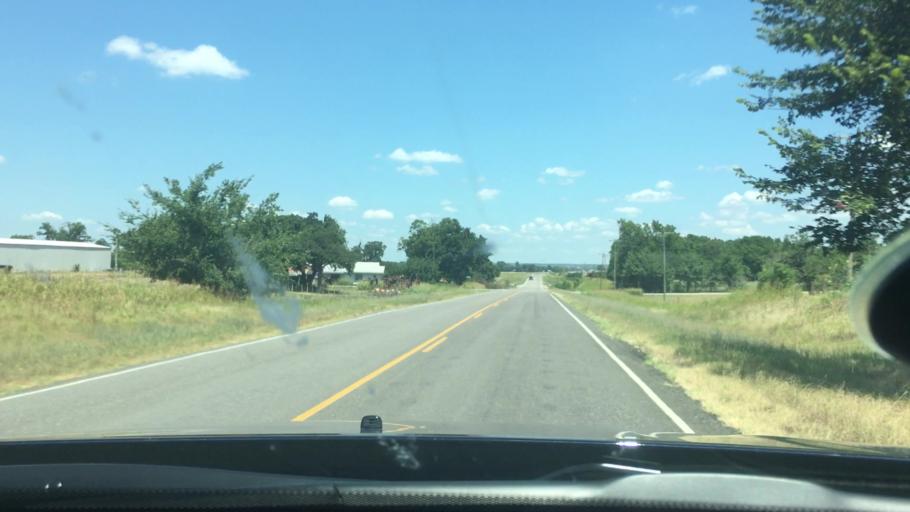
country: US
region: Oklahoma
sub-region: Carter County
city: Dickson
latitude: 34.2145
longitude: -96.9771
